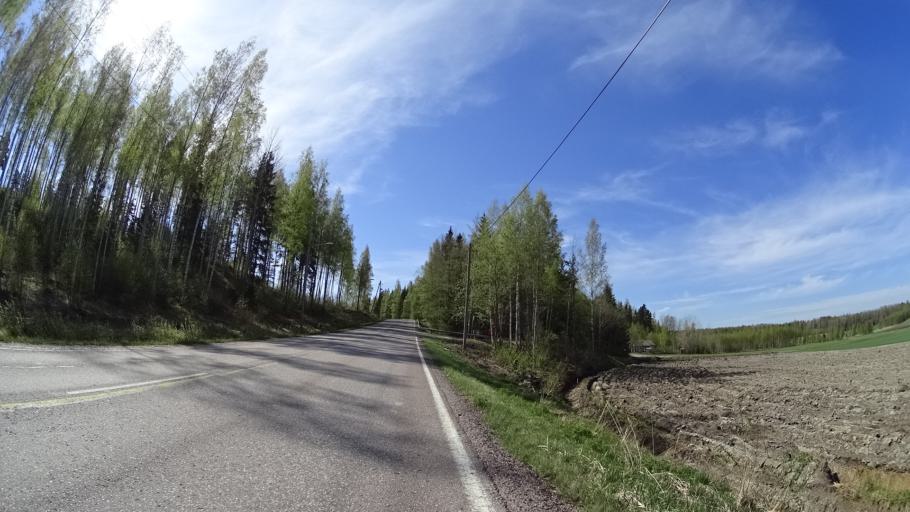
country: FI
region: Uusimaa
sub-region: Helsinki
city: Nurmijaervi
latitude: 60.3736
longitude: 24.8375
